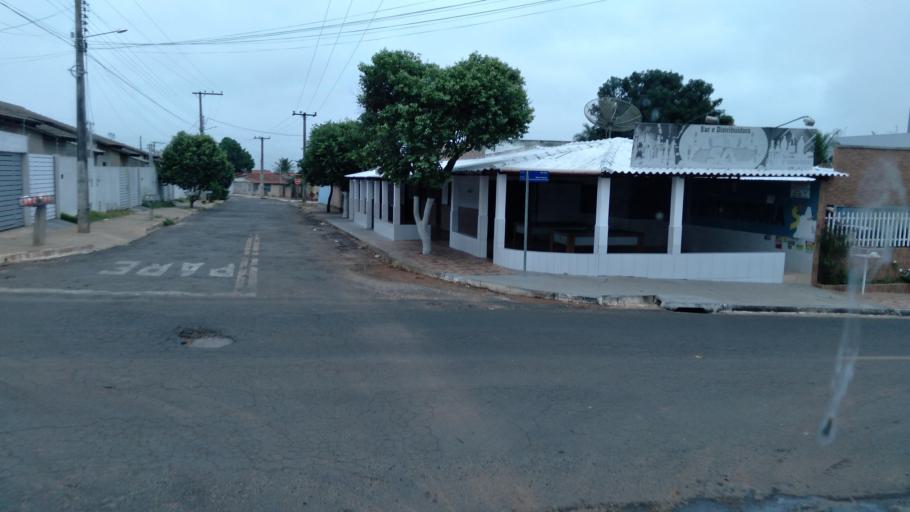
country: BR
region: Goias
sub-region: Mineiros
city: Mineiros
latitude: -17.5793
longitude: -52.5479
